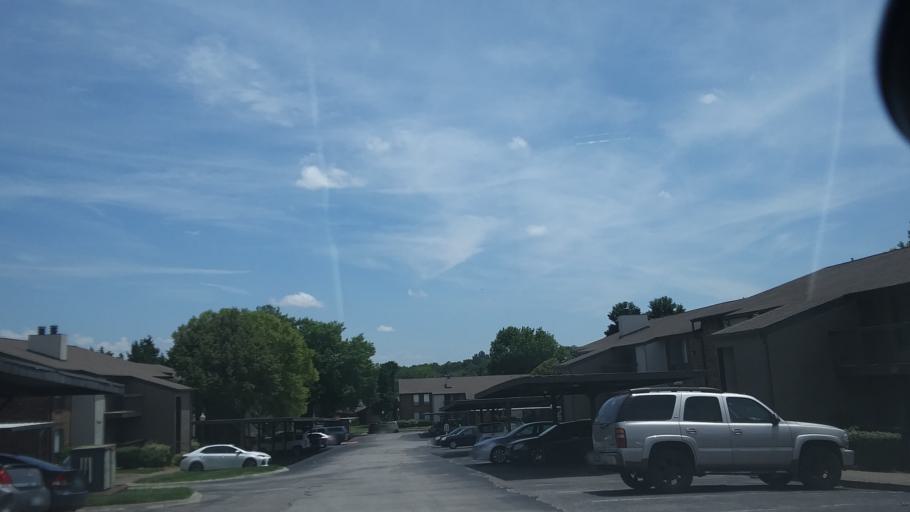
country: US
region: Tennessee
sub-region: Rutherford County
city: La Vergne
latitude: 36.0919
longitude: -86.6360
